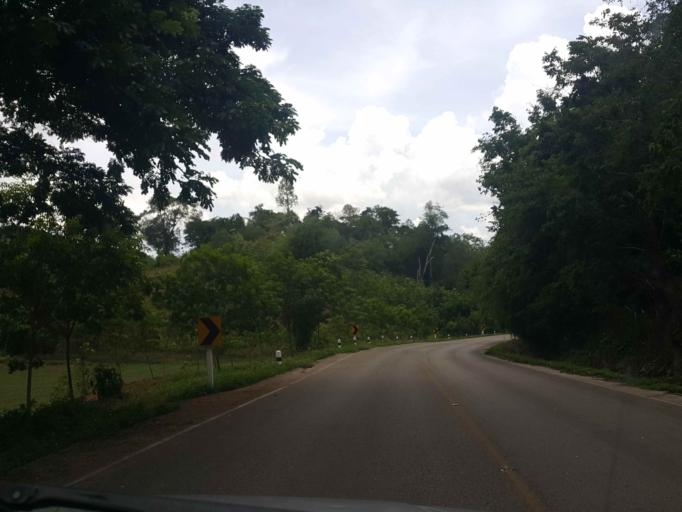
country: TH
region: Phayao
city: Chiang Muan
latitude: 18.9143
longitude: 100.1158
